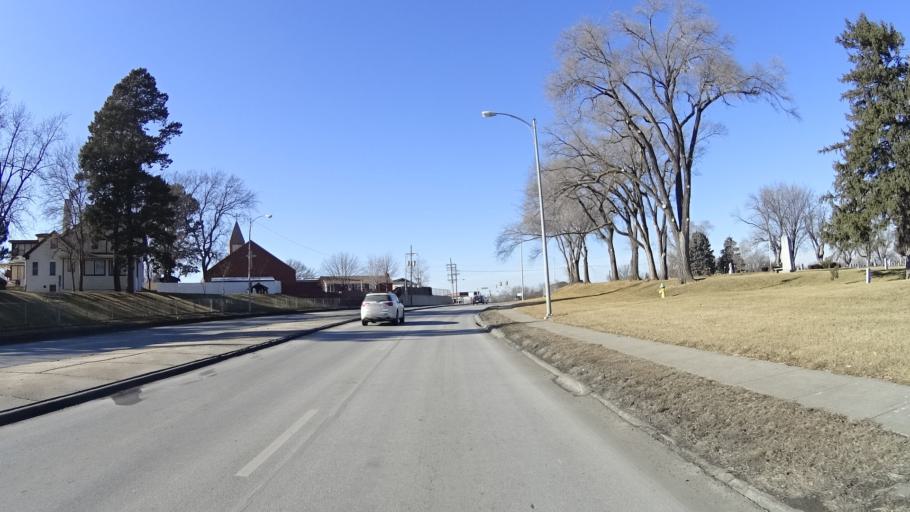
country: US
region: Nebraska
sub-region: Douglas County
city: Ralston
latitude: 41.3016
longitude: -96.0316
